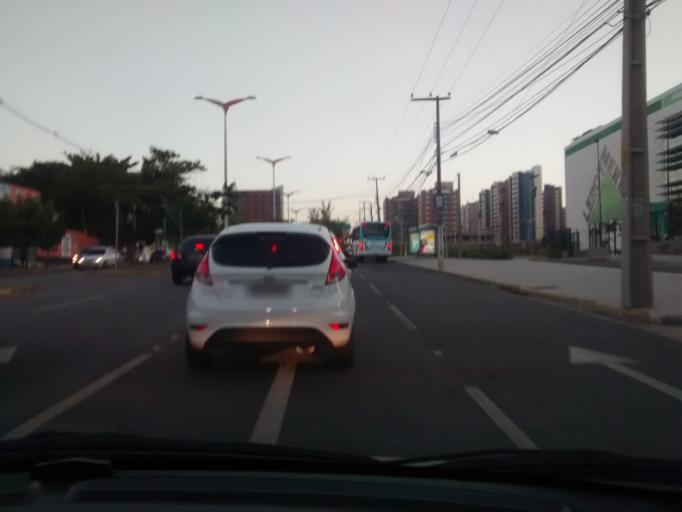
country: BR
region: Ceara
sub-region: Fortaleza
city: Fortaleza
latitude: -3.7574
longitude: -38.4833
